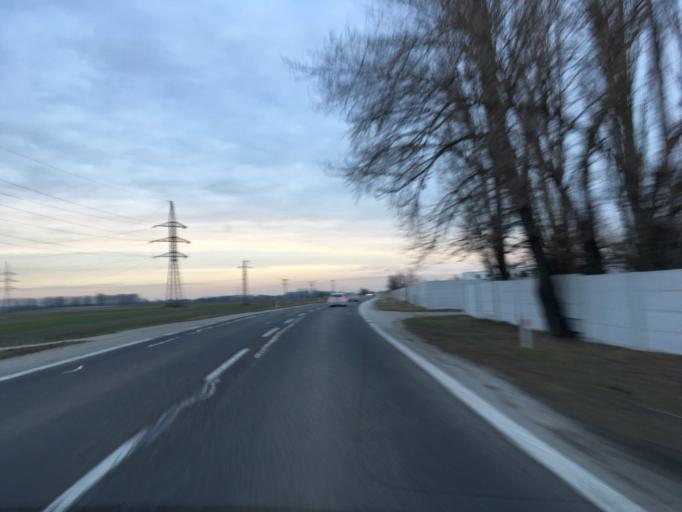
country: SK
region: Trnavsky
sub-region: Okres Dunajska Streda
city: Velky Meder
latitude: 47.8792
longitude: 17.7545
